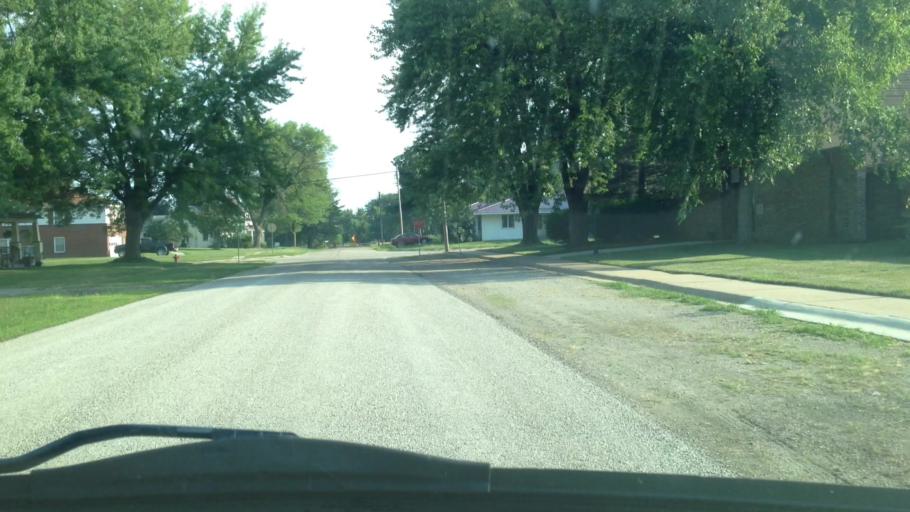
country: US
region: Iowa
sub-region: Henry County
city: Winfield
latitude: 41.2147
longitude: -91.5376
